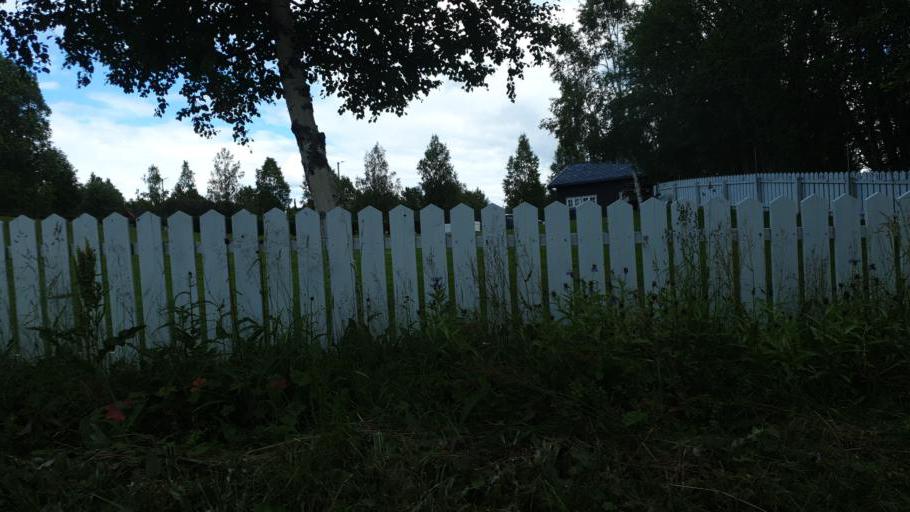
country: NO
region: Sor-Trondelag
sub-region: Rennebu
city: Berkak
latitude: 62.8297
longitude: 10.0034
